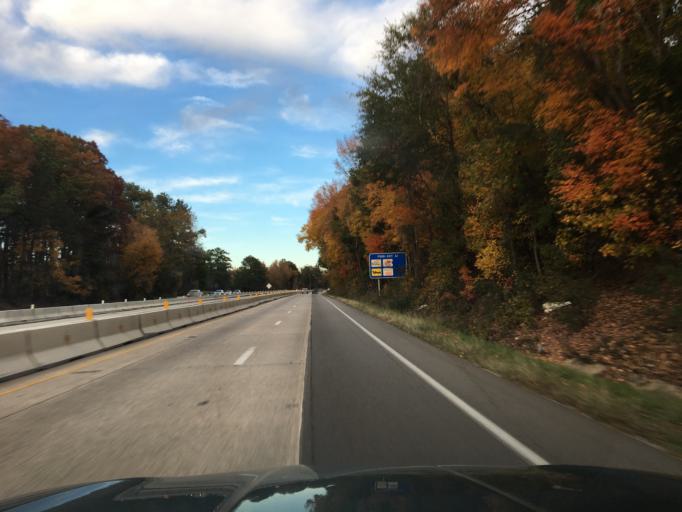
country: US
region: South Carolina
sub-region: Lexington County
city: Oak Grove
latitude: 33.9984
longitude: -81.1744
